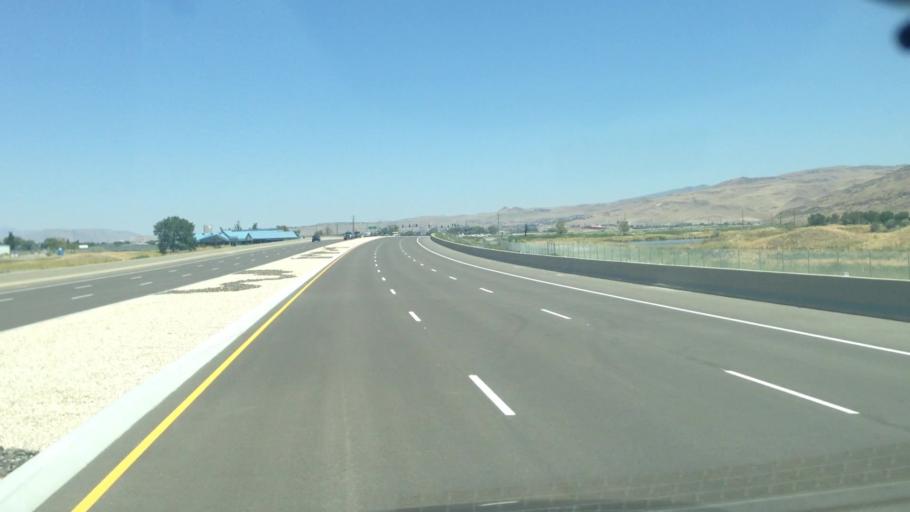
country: US
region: Nevada
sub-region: Washoe County
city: Sparks
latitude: 39.4939
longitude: -119.7316
